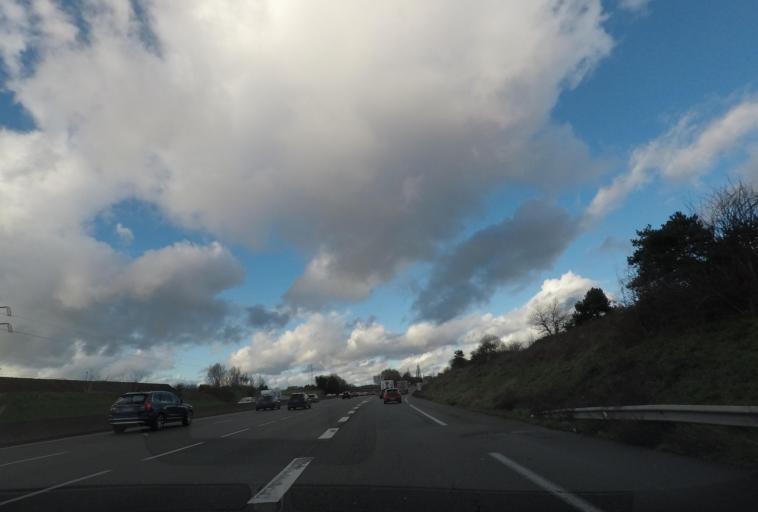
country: FR
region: Ile-de-France
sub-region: Departement de l'Essonne
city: Ormoy
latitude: 48.5691
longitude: 2.4711
